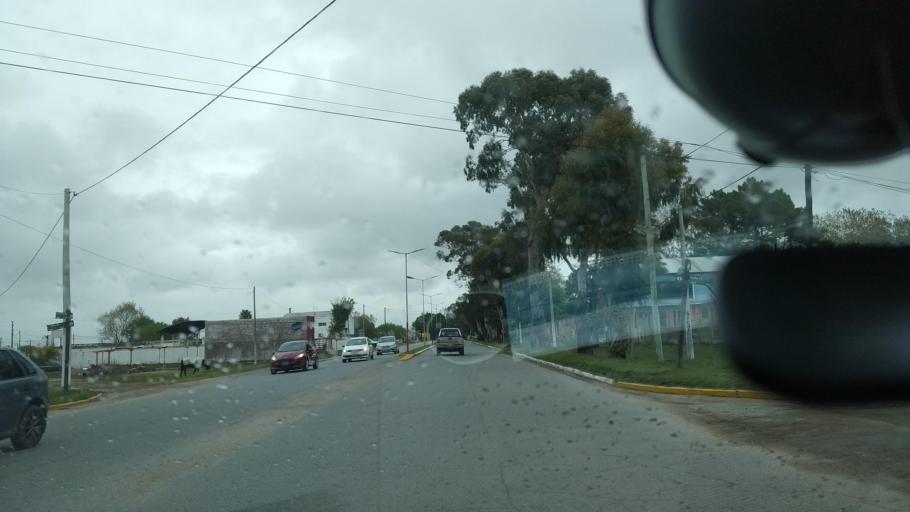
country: AR
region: Buenos Aires
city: San Clemente del Tuyu
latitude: -36.3827
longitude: -56.7234
